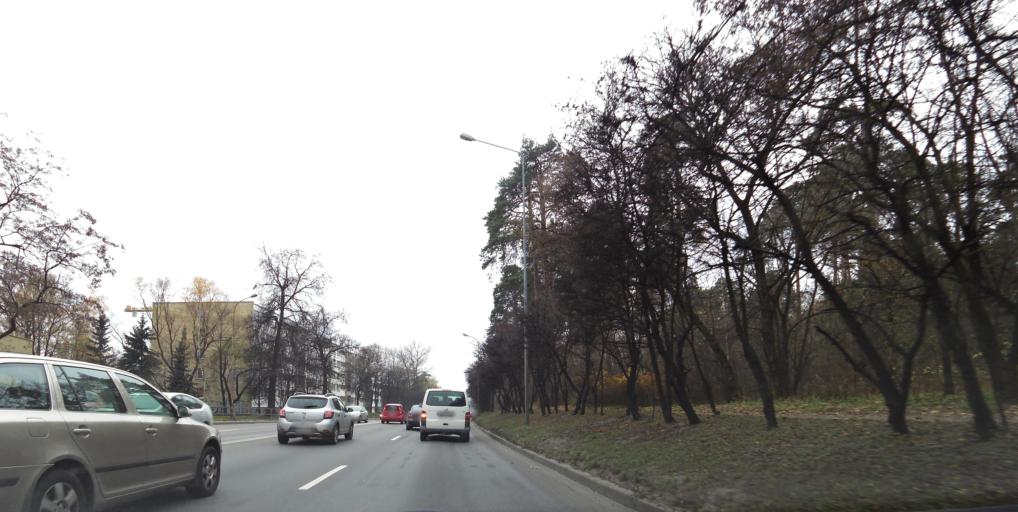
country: LT
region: Vilnius County
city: Vilkpede
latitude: 54.6757
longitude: 25.2446
